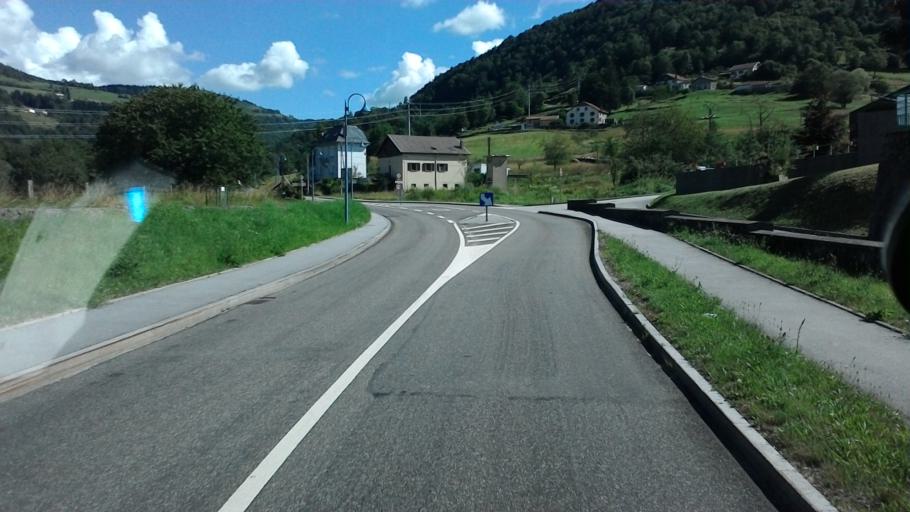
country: FR
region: Lorraine
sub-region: Departement des Vosges
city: Cornimont
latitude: 47.9732
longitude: 6.8315
